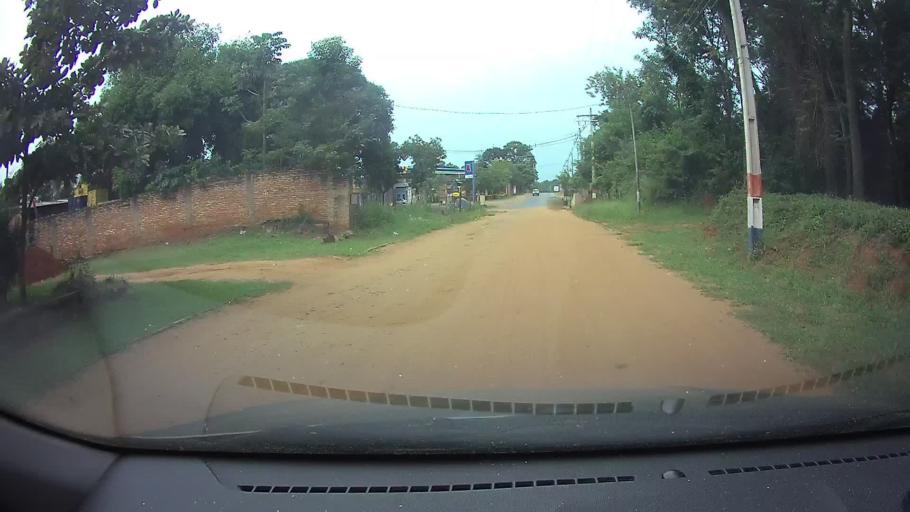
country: PY
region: Central
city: Limpio
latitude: -25.2198
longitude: -57.4789
